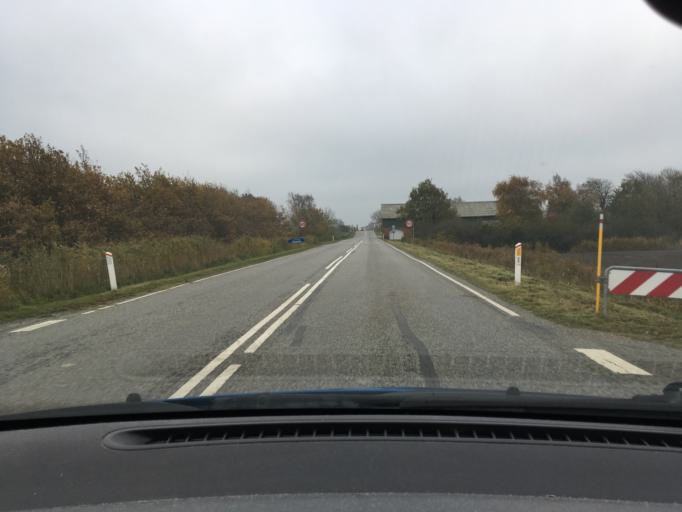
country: DE
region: Schleswig-Holstein
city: Aventoft
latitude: 54.9143
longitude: 8.8327
